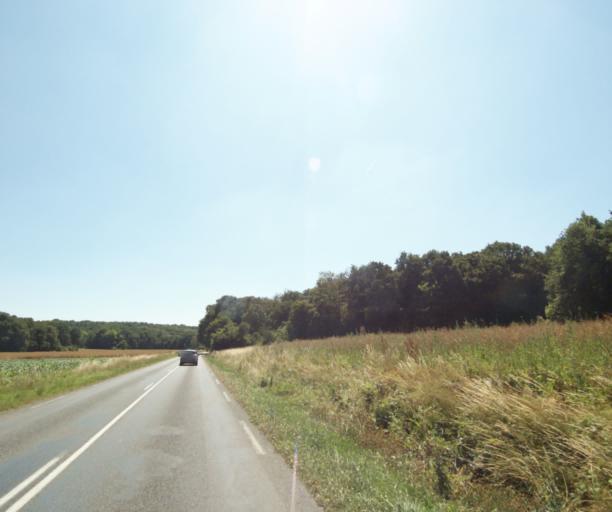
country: FR
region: Ile-de-France
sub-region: Departement de l'Essonne
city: Milly-la-Foret
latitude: 48.3679
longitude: 2.4707
